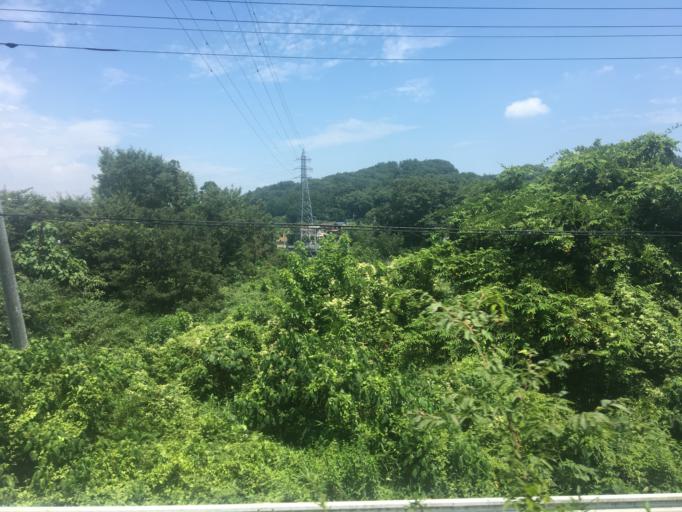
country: JP
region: Saitama
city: Yorii
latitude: 36.0984
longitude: 139.1936
